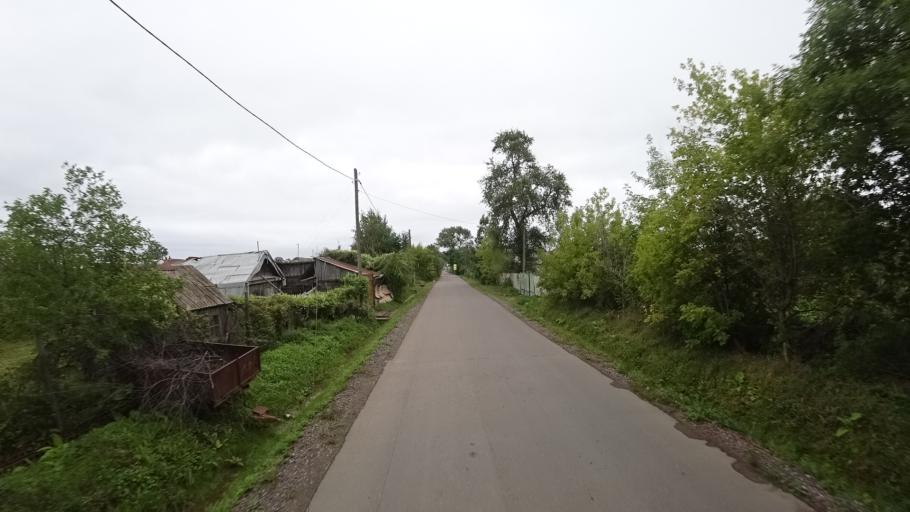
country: RU
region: Primorskiy
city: Chernigovka
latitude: 44.3370
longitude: 132.5396
